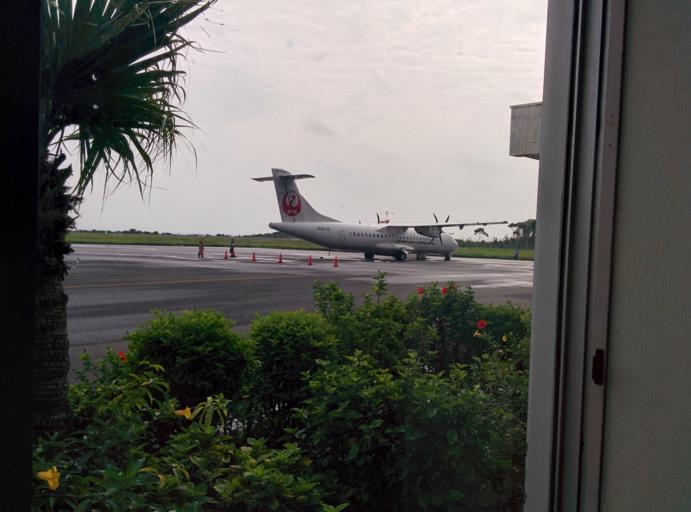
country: JP
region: Kagoshima
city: Kagoshima-shi
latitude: 31.6008
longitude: 130.5580
